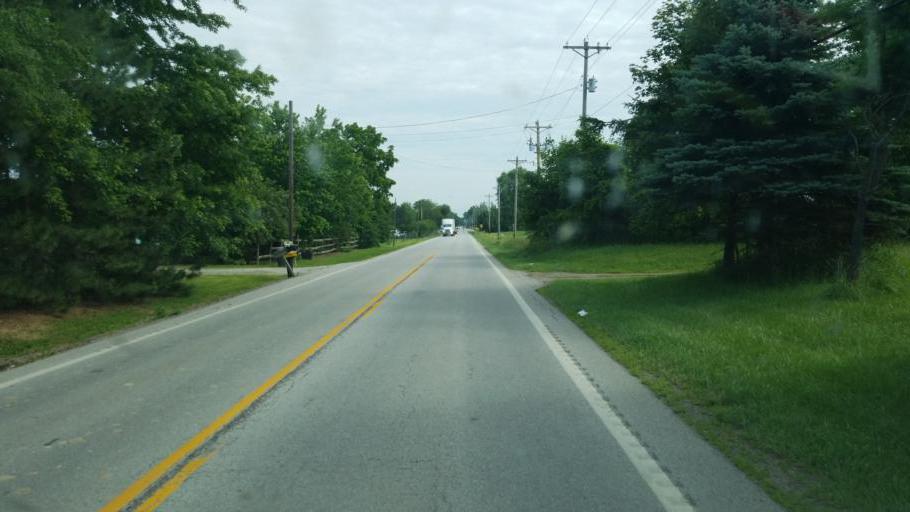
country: US
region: Ohio
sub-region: Medina County
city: Lodi
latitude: 41.1546
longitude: -82.0233
